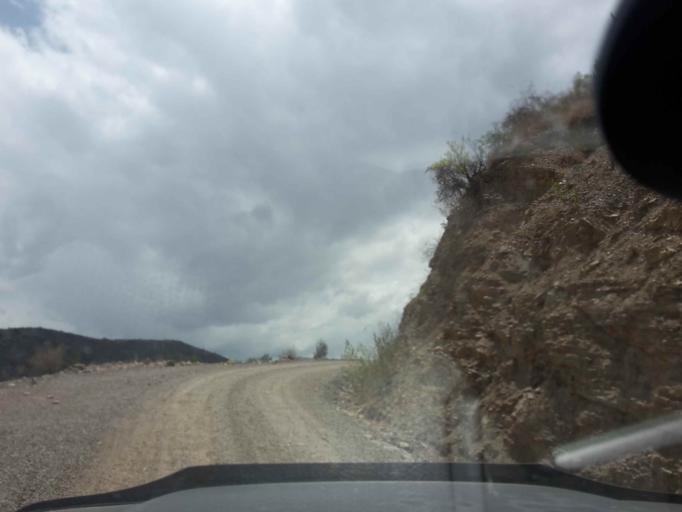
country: BO
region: Cochabamba
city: Sipe Sipe
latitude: -17.5509
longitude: -66.4772
